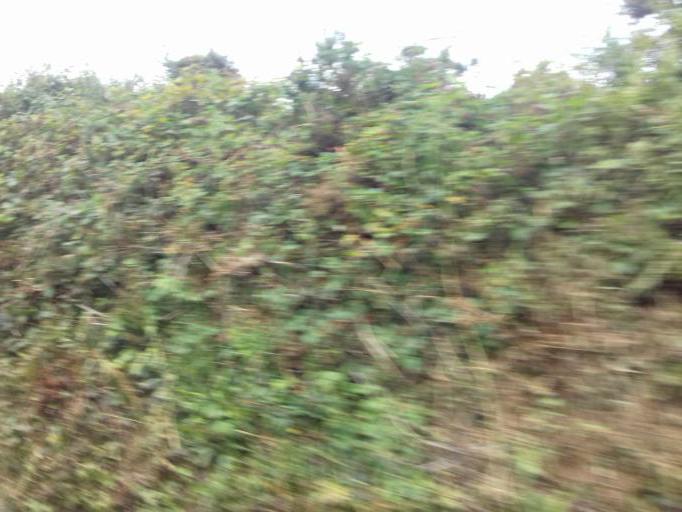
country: IE
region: Leinster
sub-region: Loch Garman
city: Bunclody
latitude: 52.6565
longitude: -6.7619
